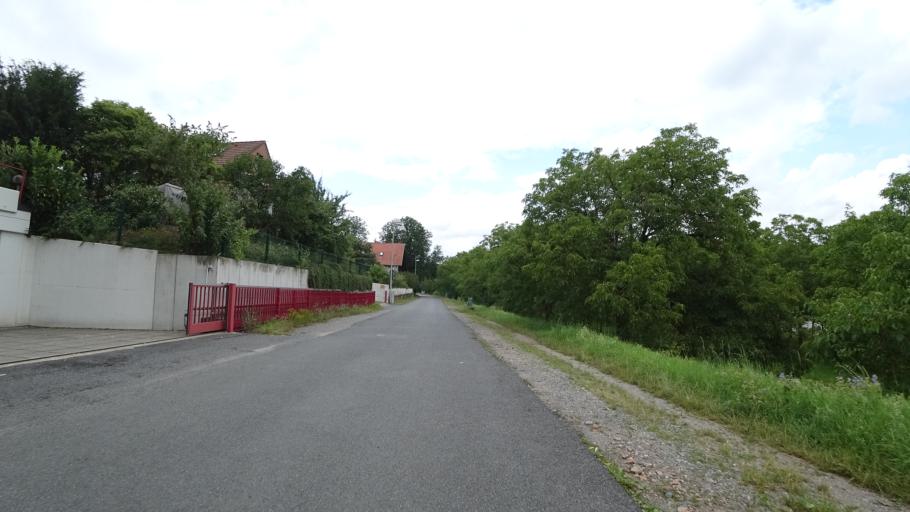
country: DE
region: Bavaria
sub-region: Regierungsbezirk Unterfranken
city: Miltenberg
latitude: 49.7045
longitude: 9.2544
